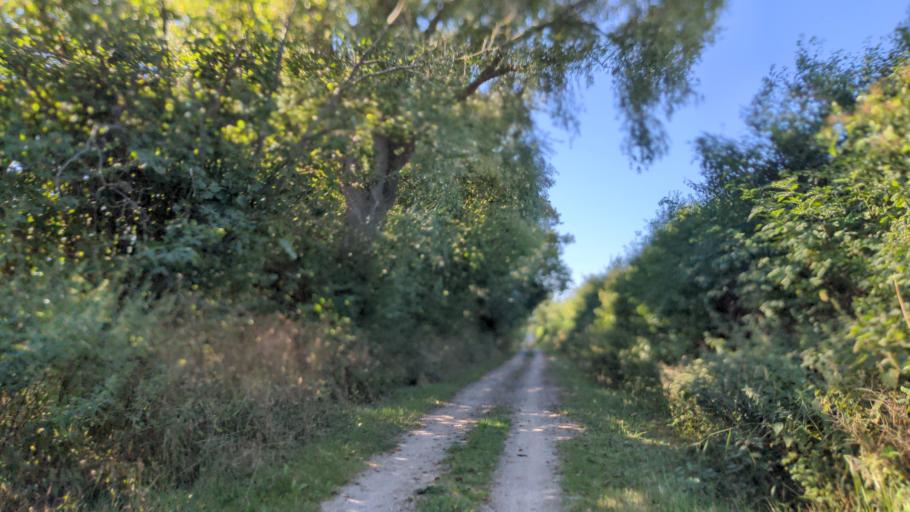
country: DE
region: Mecklenburg-Vorpommern
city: Ostseebad Boltenhagen
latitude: 53.9638
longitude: 11.2355
